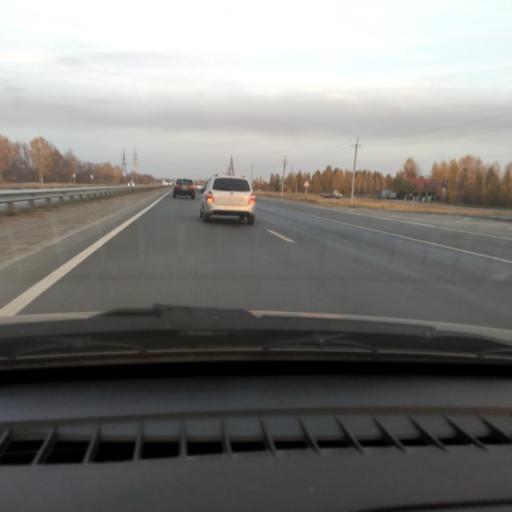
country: RU
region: Samara
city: Tol'yatti
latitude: 53.5771
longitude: 49.4257
